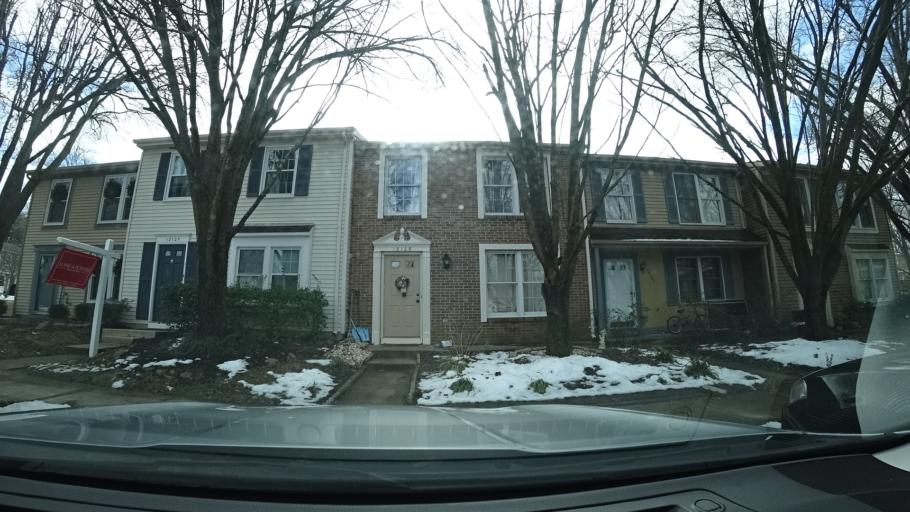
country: US
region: Virginia
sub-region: Fairfax County
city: Herndon
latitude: 38.9736
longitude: -77.3639
